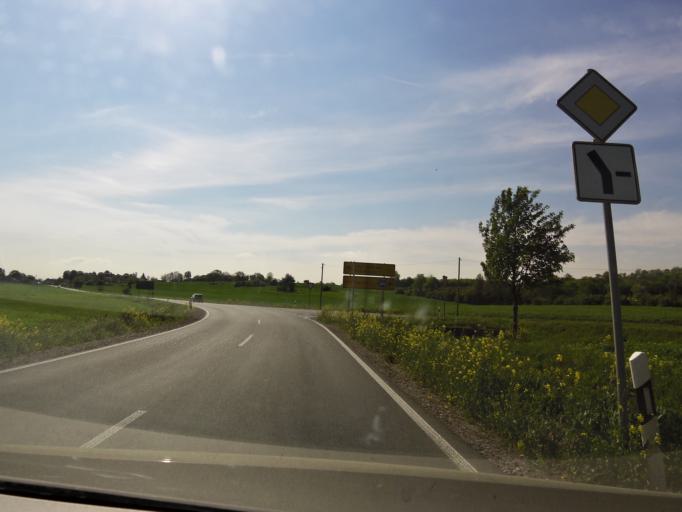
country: DE
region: Thuringia
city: Elxleben
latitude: 51.0354
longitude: 10.9596
